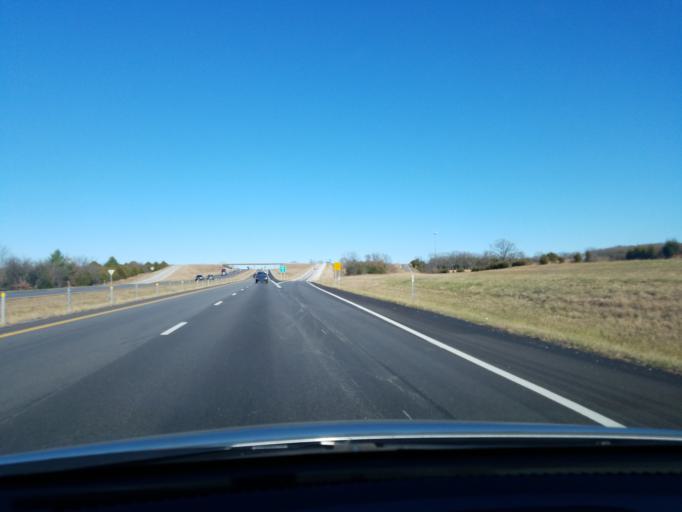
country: US
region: Missouri
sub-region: Webster County
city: Marshfield
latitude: 37.4230
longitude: -92.8830
